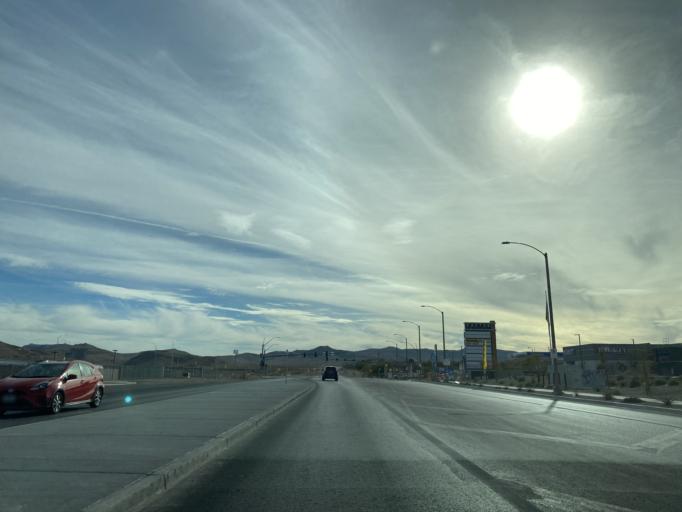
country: US
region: Nevada
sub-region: Clark County
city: Enterprise
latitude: 36.0005
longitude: -115.2436
